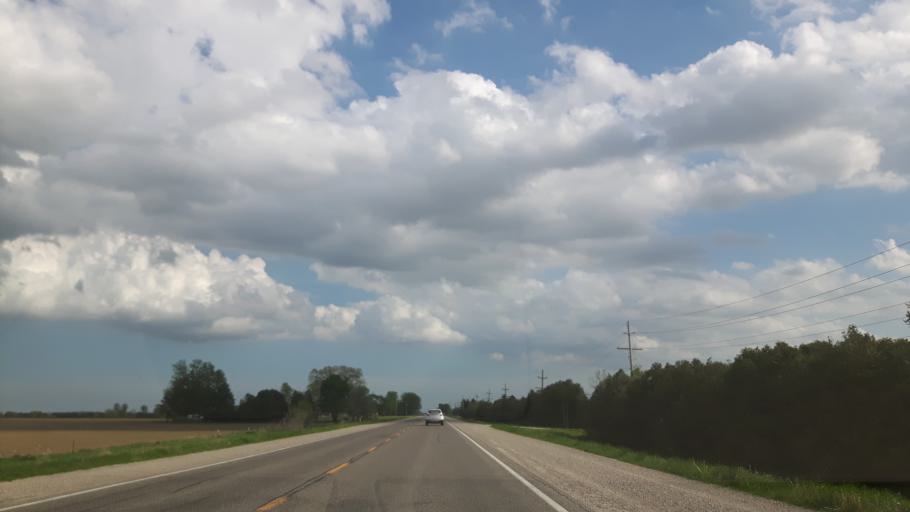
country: CA
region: Ontario
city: South Huron
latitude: 43.2628
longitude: -81.4638
